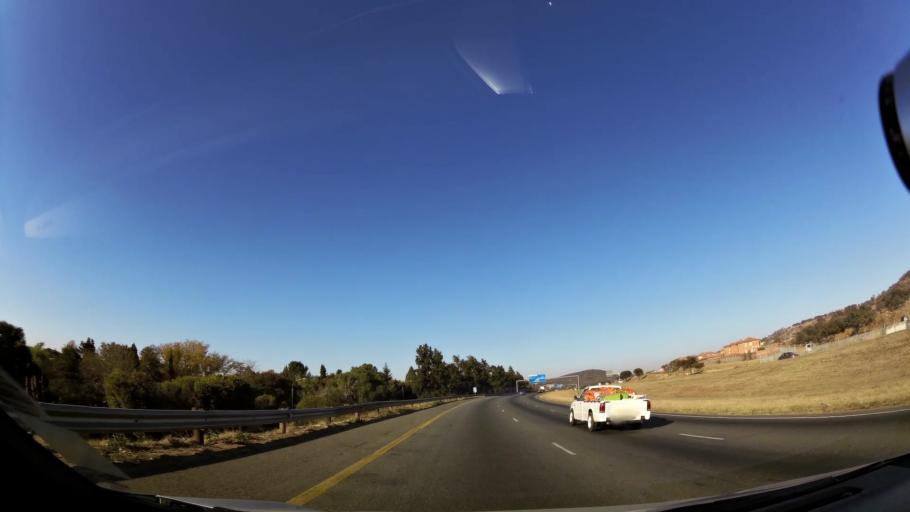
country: ZA
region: Gauteng
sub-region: Ekurhuleni Metropolitan Municipality
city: Germiston
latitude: -26.2780
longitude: 28.1042
